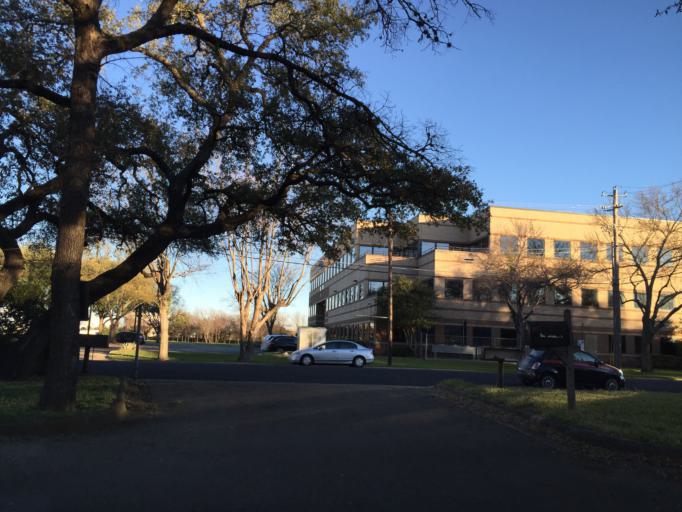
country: US
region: Texas
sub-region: Williamson County
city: Jollyville
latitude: 30.4365
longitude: -97.7761
